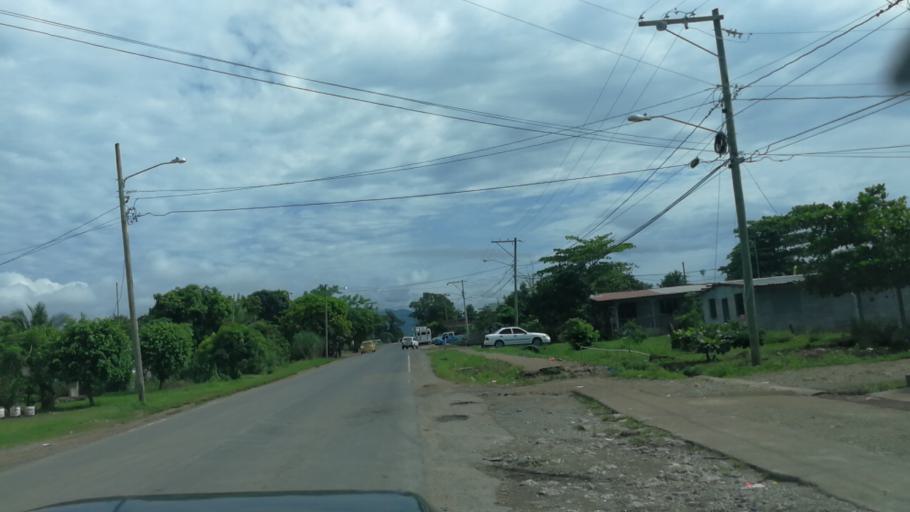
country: PA
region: Panama
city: Paso Blanco
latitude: 9.1252
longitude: -79.2526
